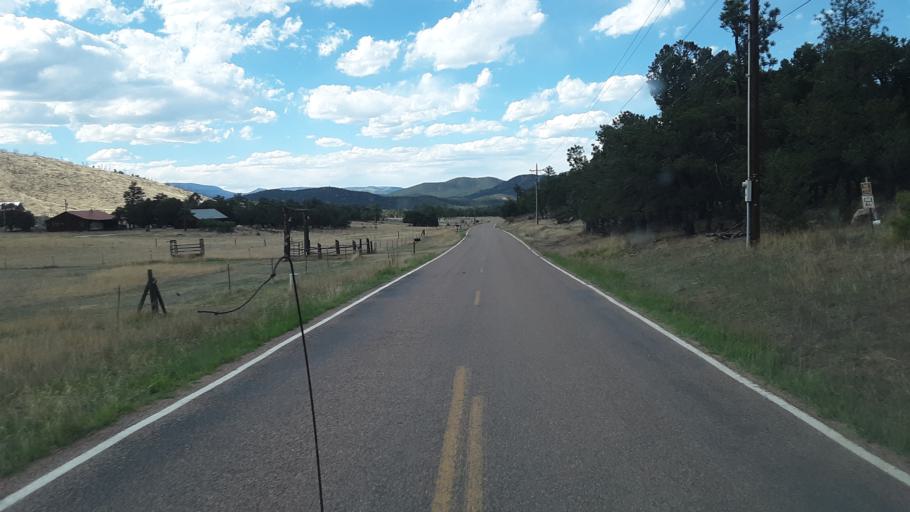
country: US
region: Colorado
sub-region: Custer County
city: Westcliffe
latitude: 38.3297
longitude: -105.4851
